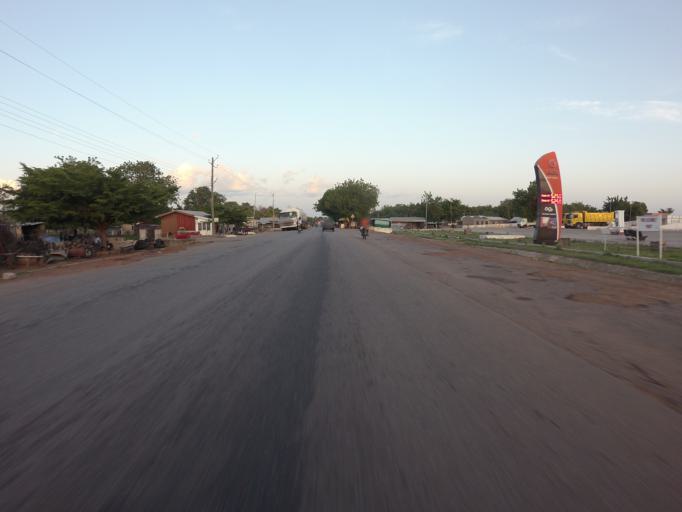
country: GH
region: Upper East
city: Navrongo
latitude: 10.8945
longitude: -1.0832
